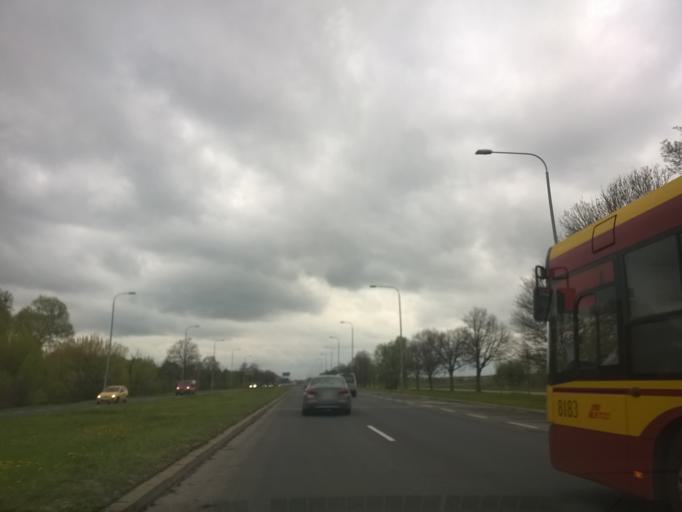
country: PL
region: Masovian Voivodeship
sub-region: Warszawa
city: Wilanow
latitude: 52.1465
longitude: 21.0938
